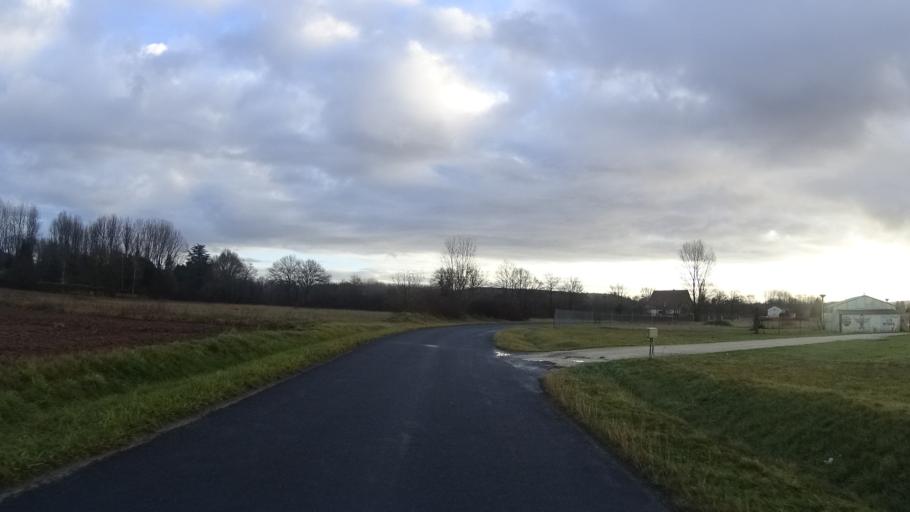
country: FR
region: Aquitaine
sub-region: Departement de la Dordogne
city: Bassillac
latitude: 45.2021
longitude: 0.8134
